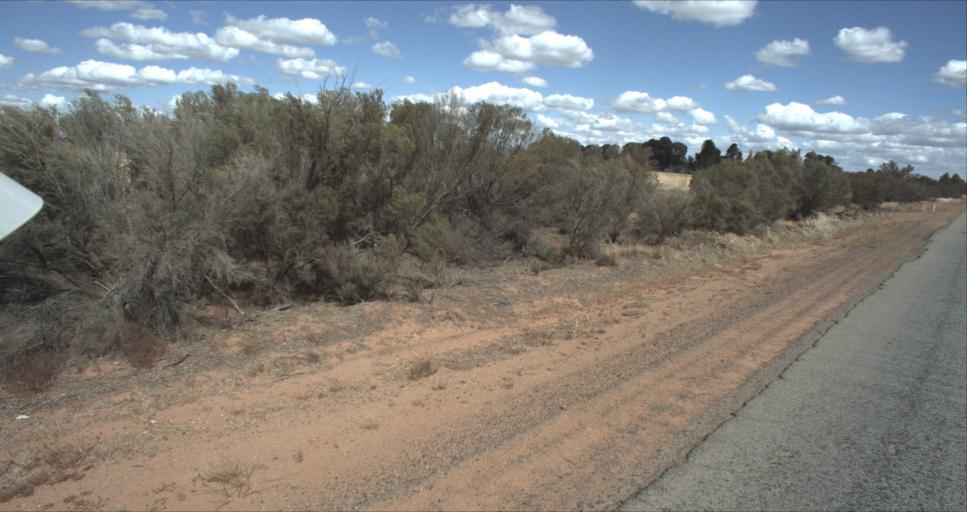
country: AU
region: New South Wales
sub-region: Leeton
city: Leeton
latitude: -34.4783
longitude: 146.2496
